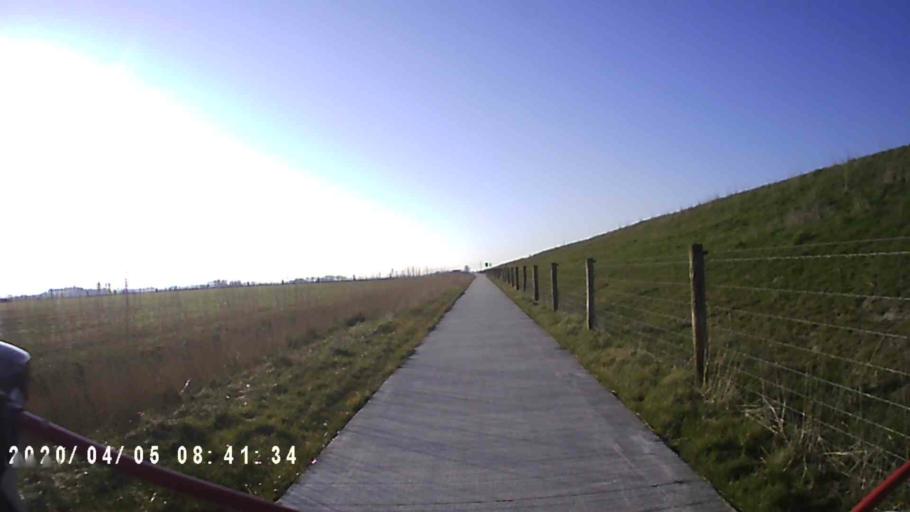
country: NL
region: Groningen
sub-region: Gemeente Winsum
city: Winsum
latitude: 53.3101
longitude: 6.4906
